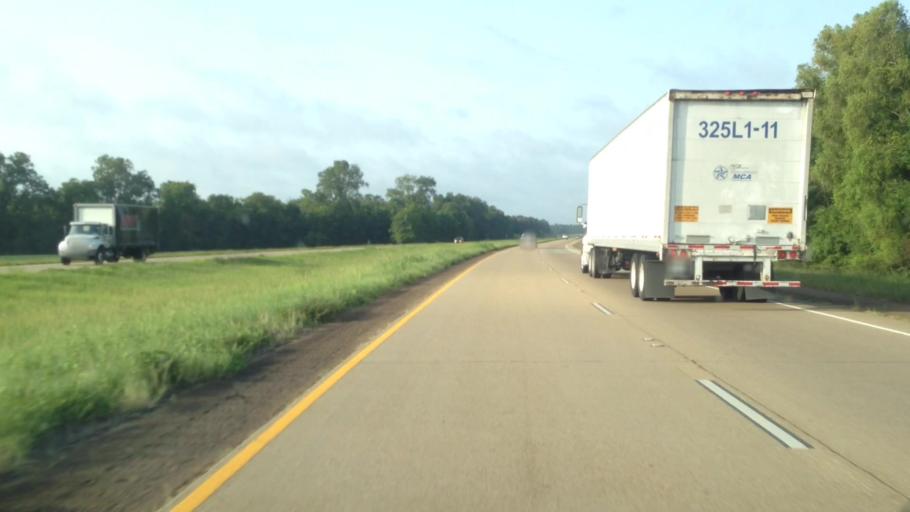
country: US
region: Louisiana
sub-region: Rapides Parish
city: Lecompte
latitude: 31.1203
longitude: -92.4425
